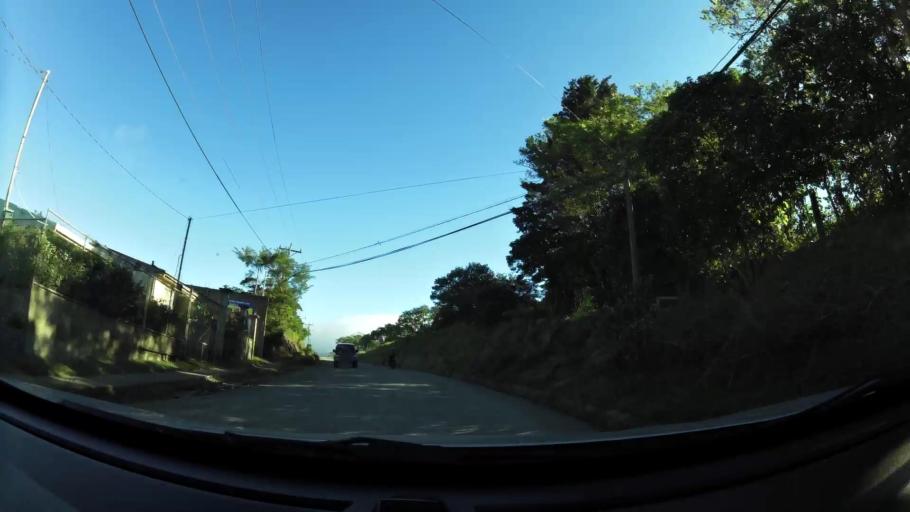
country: CR
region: Guanacaste
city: Juntas
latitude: 10.3033
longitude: -84.8339
